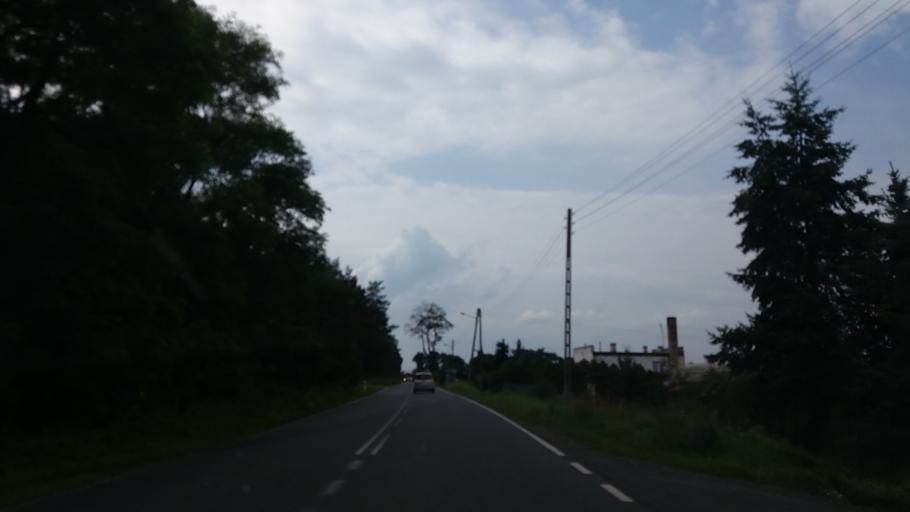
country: PL
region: Lubusz
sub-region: Powiat strzelecko-drezdenecki
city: Zwierzyn
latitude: 52.7247
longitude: 15.5754
